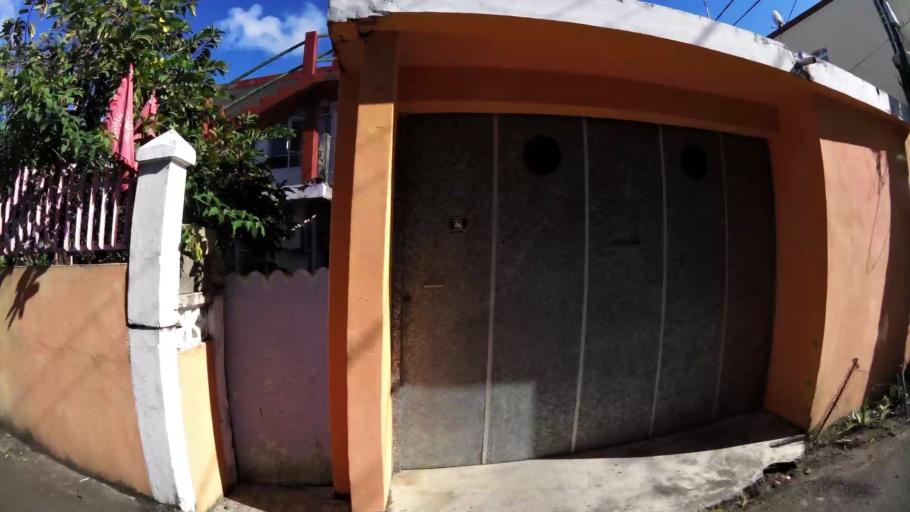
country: MU
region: Grand Port
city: Mahebourg
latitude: -20.4129
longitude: 57.7071
